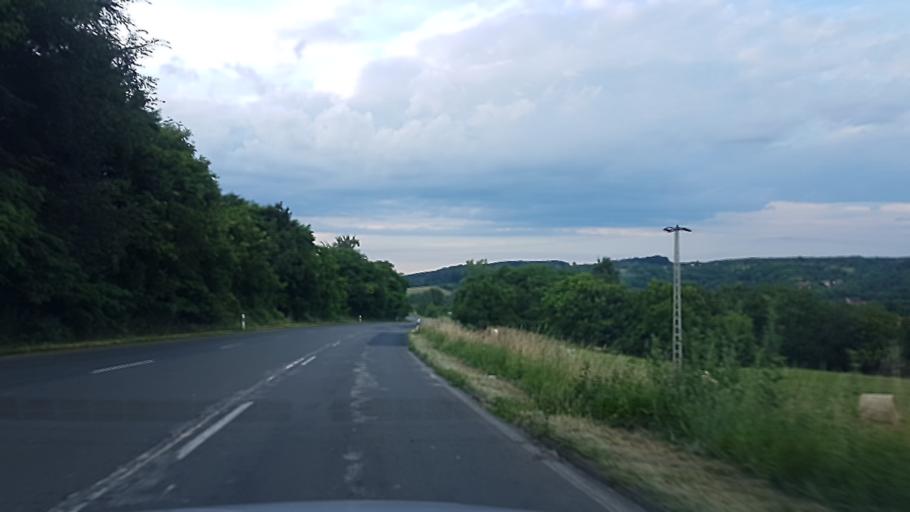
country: HU
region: Somogy
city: Kaposvar
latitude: 46.2760
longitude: 17.8216
